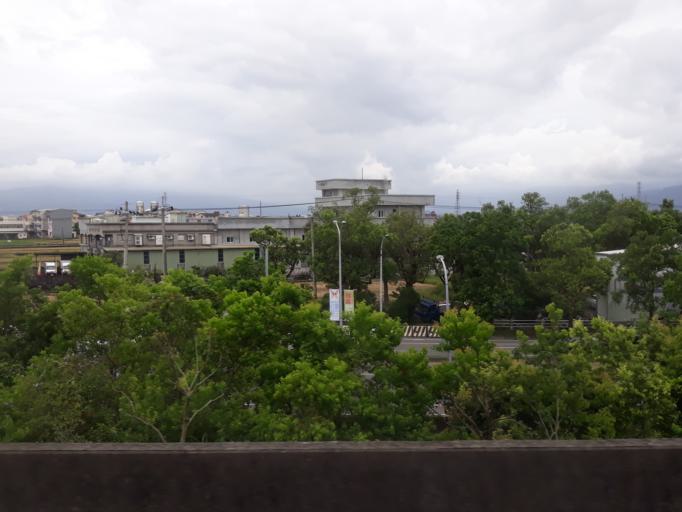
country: TW
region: Taiwan
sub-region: Yilan
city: Yilan
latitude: 24.7213
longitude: 121.7707
